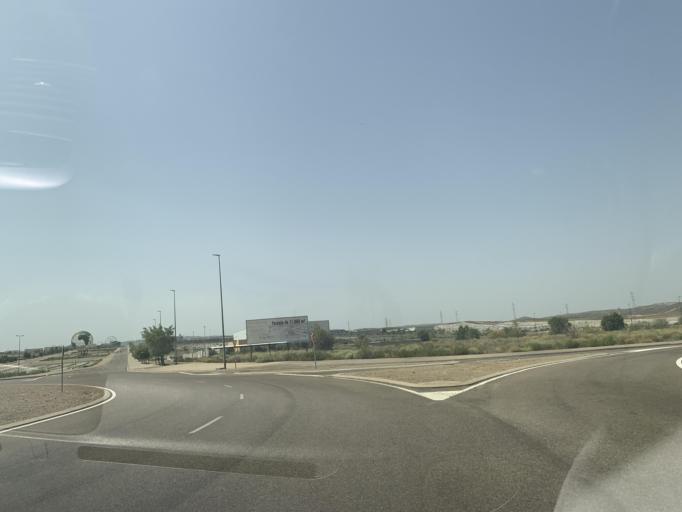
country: ES
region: Aragon
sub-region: Provincia de Zaragoza
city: Zaragoza
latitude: 41.5830
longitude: -0.8416
